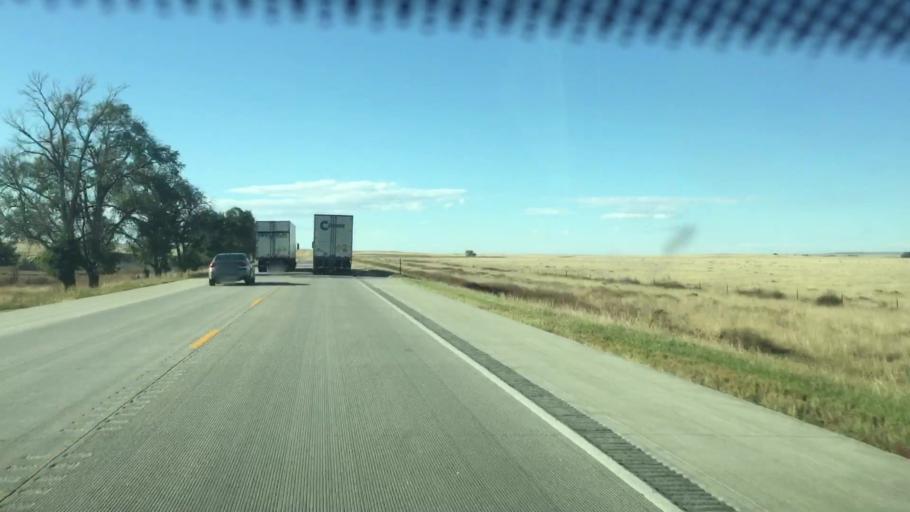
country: US
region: Colorado
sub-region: Lincoln County
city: Hugo
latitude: 38.9368
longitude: -103.2055
